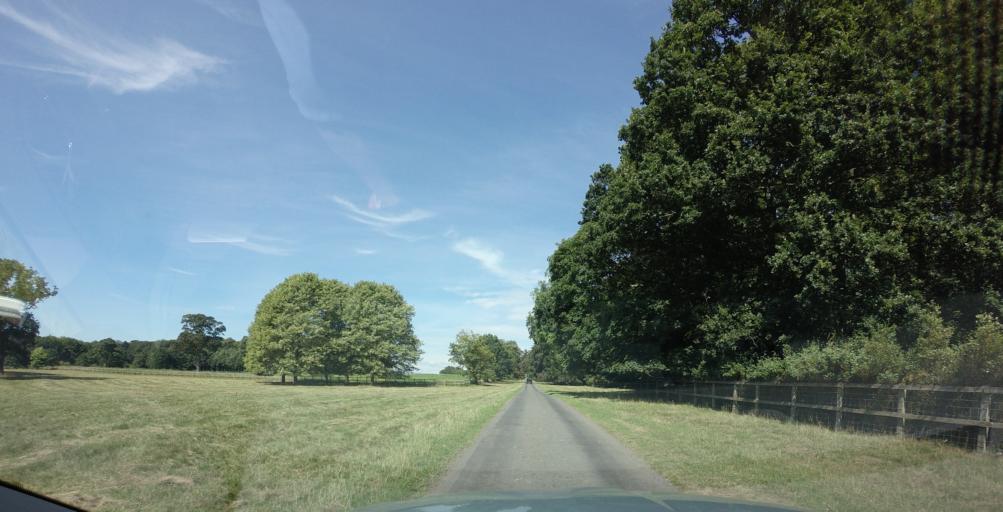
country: GB
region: England
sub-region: North Yorkshire
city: Ripon
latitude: 54.1081
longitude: -1.4705
